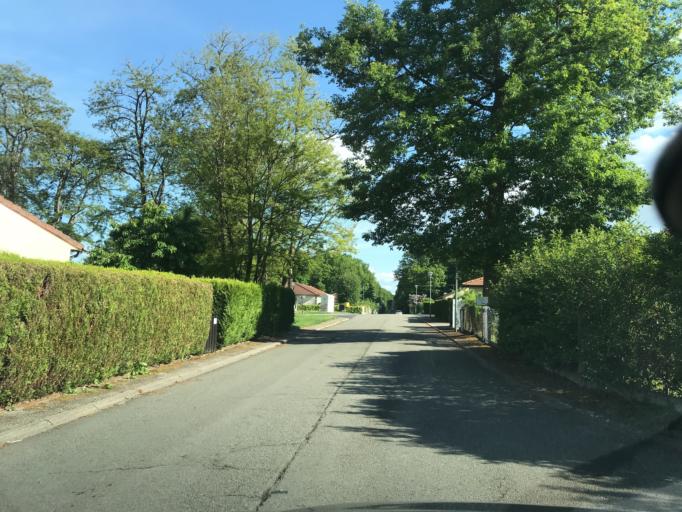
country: FR
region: Haute-Normandie
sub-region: Departement de l'Eure
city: Evreux
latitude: 49.0119
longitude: 1.1369
